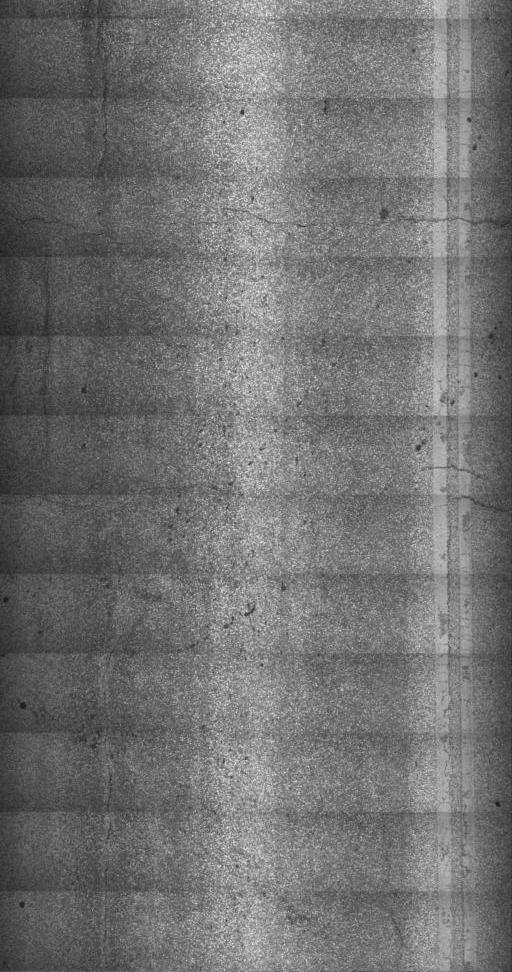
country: US
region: Vermont
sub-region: Lamoille County
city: Morristown
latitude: 44.4691
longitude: -72.6878
